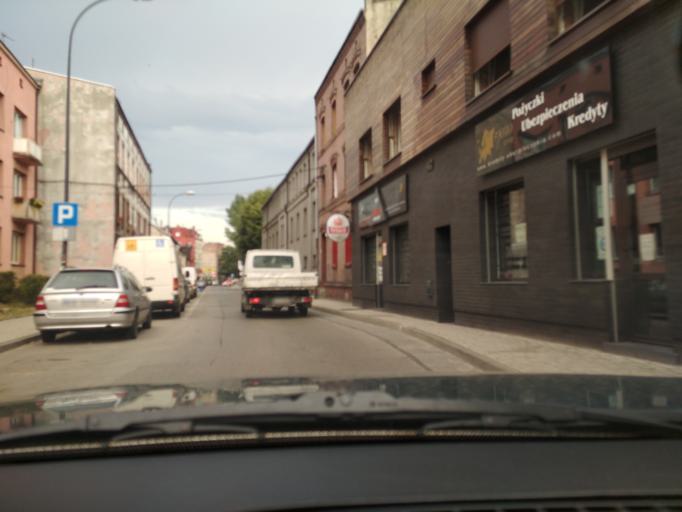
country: PL
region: Silesian Voivodeship
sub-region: Swietochlowice
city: Swietochlowice
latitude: 50.2905
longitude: 18.9160
